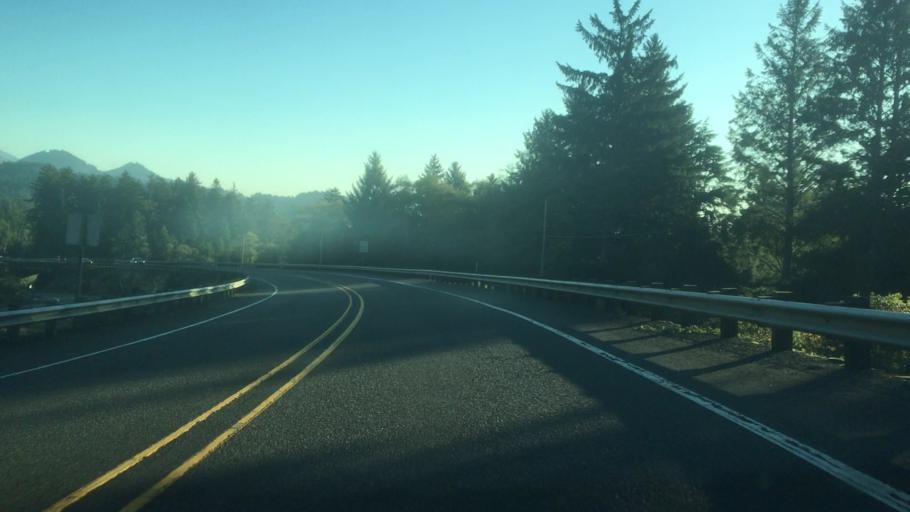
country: US
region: Oregon
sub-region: Clatsop County
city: Cannon Beach
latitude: 45.9063
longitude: -123.9539
